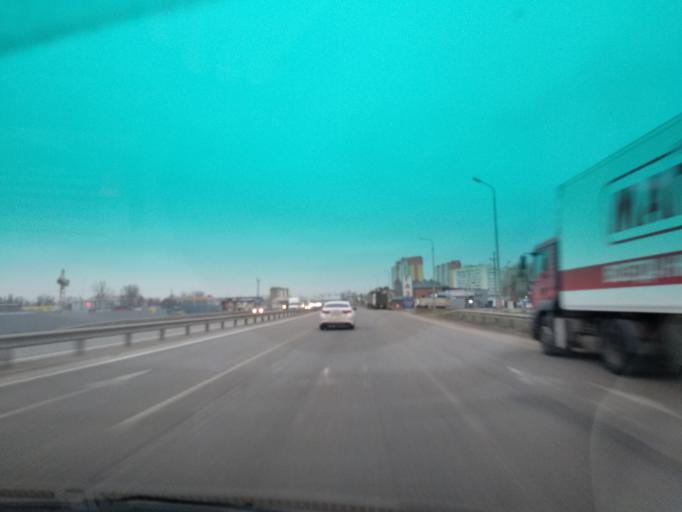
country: RU
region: Krasnodarskiy
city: Pashkovskiy
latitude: 45.0381
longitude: 39.1282
